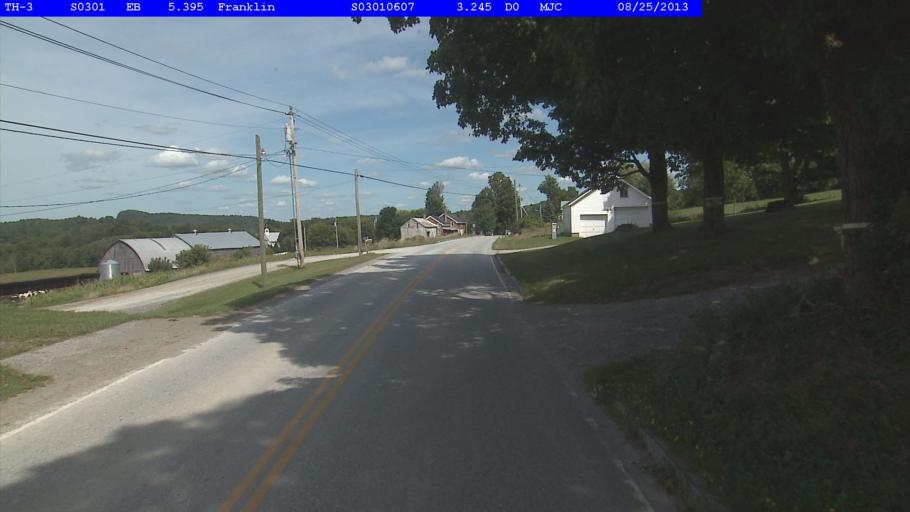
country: US
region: Vermont
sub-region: Franklin County
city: Enosburg Falls
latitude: 44.9796
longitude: -72.9223
